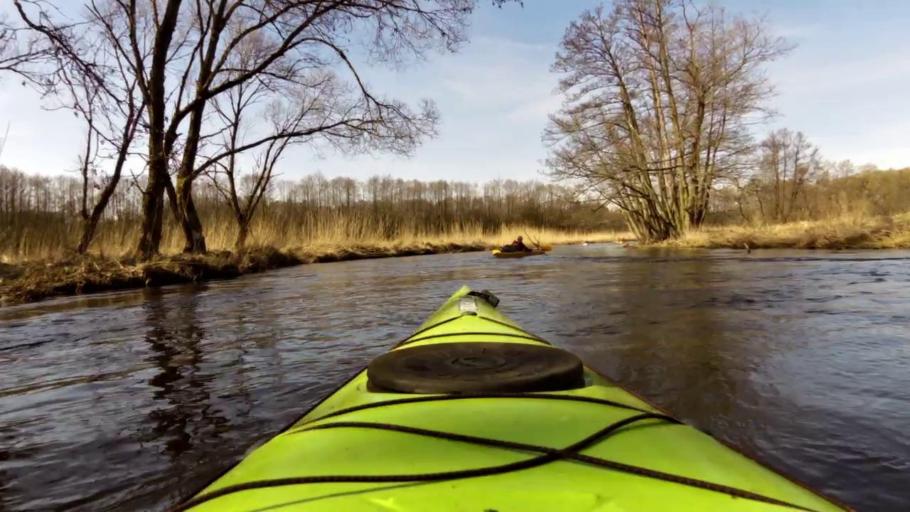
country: PL
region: West Pomeranian Voivodeship
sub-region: Powiat lobeski
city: Lobez
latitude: 53.6671
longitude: 15.5648
